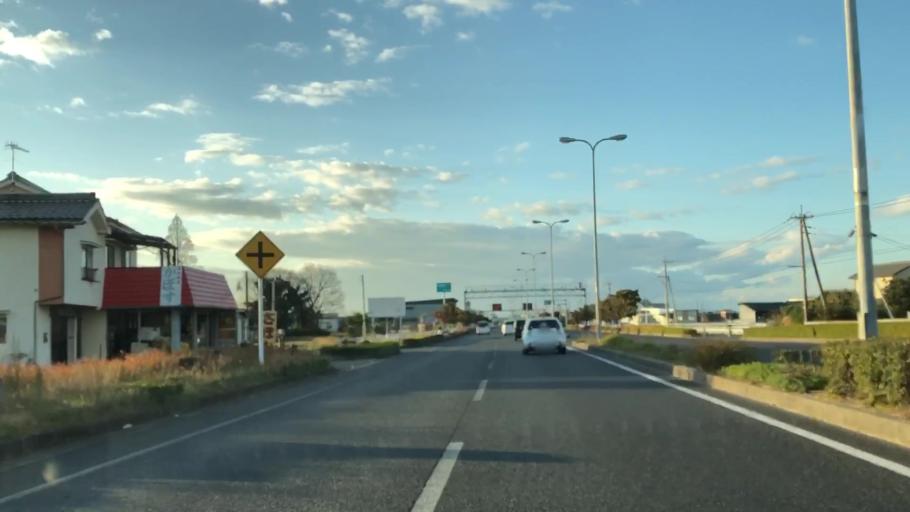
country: JP
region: Fukuoka
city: Nakatsu
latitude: 33.5446
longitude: 131.2856
